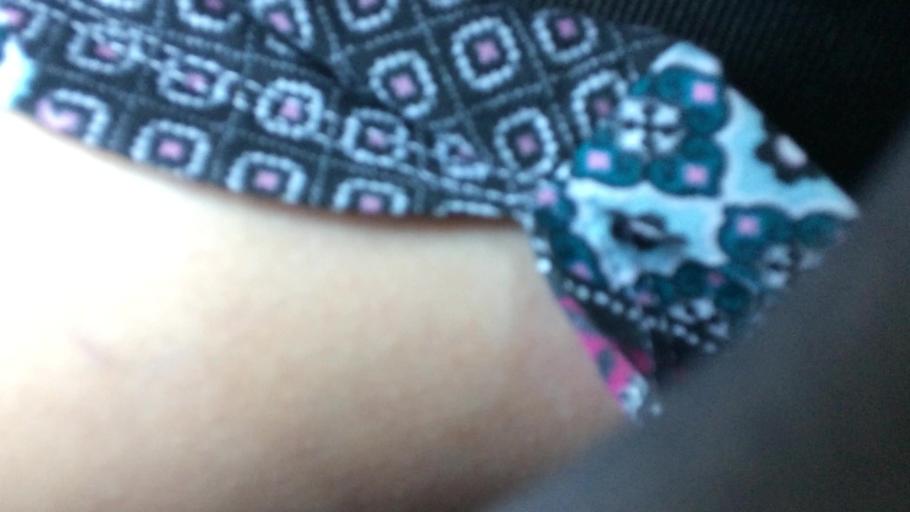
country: US
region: New Mexico
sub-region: San Miguel County
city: Las Vegas
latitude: 35.8499
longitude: -104.9293
